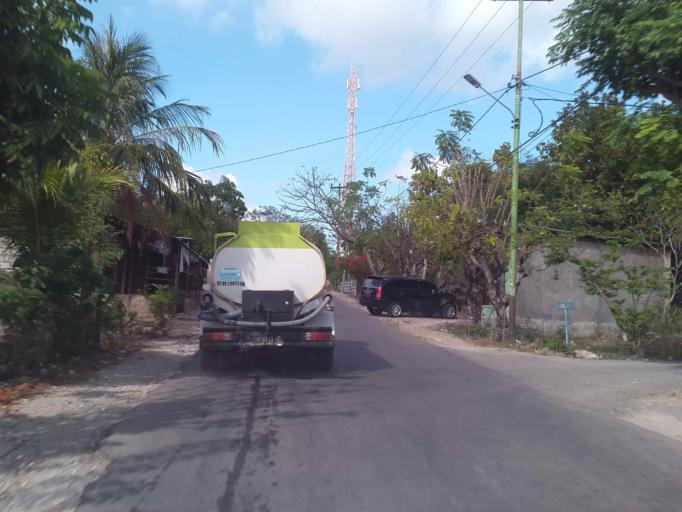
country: ID
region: East Nusa Tenggara
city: Airsagu
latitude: -10.2082
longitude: 123.5788
